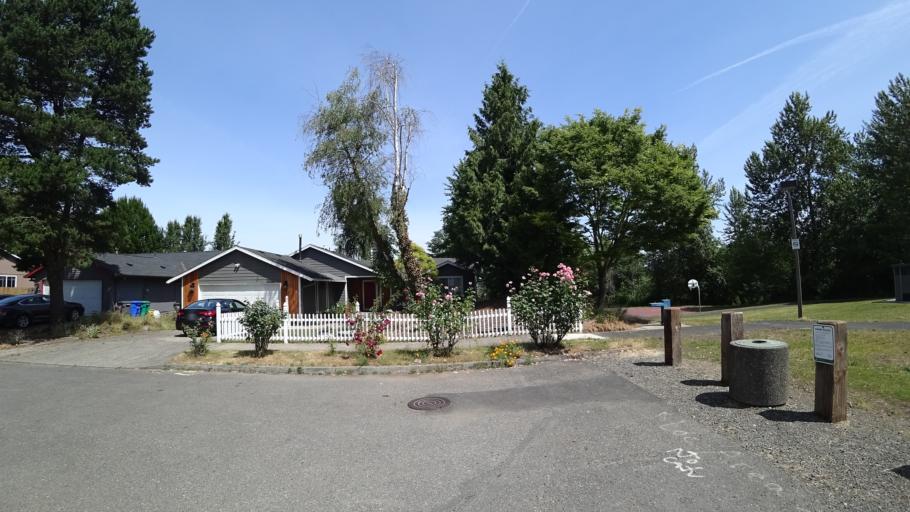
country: US
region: Oregon
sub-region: Multnomah County
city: Fairview
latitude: 45.5500
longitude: -122.5050
